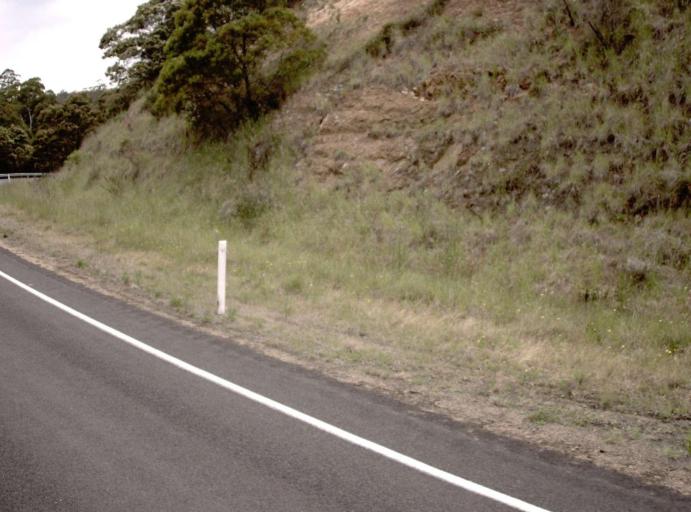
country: AU
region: New South Wales
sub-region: Bombala
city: Bombala
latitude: -37.2407
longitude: 149.2605
